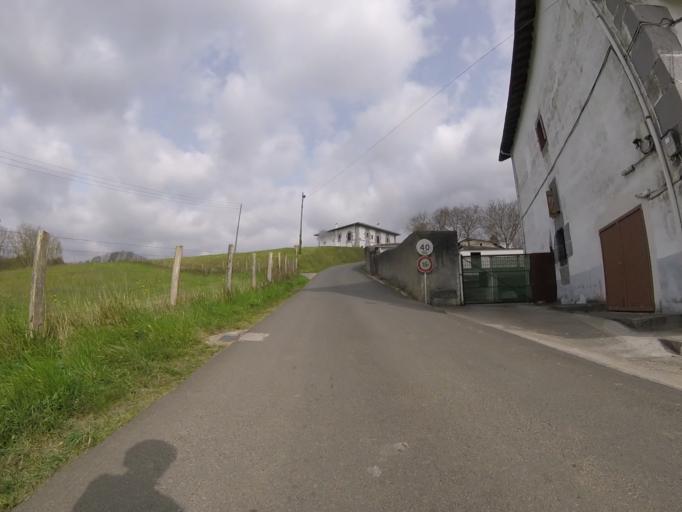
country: ES
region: Basque Country
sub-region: Provincia de Guipuzcoa
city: Zizurkil
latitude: 43.2000
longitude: -2.0749
